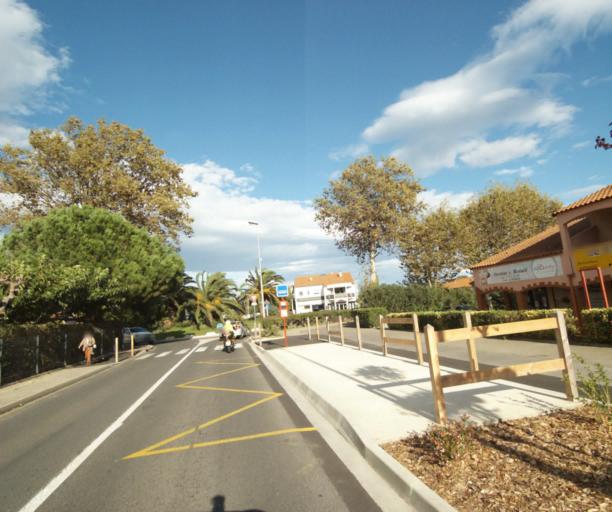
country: FR
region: Languedoc-Roussillon
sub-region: Departement des Pyrenees-Orientales
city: Argelers
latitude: 42.5489
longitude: 3.0388
